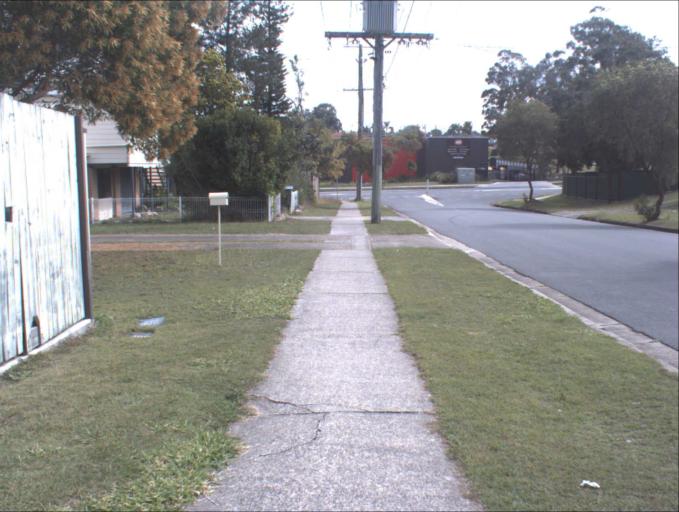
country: AU
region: Queensland
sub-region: Logan
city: Waterford West
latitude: -27.6842
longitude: 153.0946
